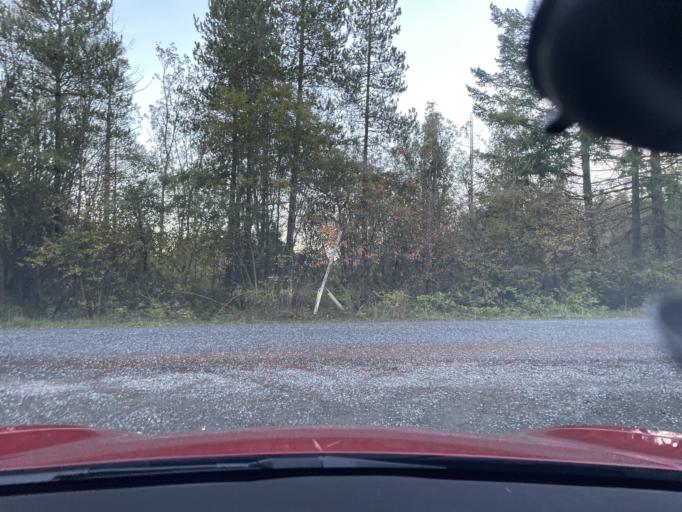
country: US
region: Washington
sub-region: San Juan County
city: Friday Harbor
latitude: 48.6141
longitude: -123.1391
